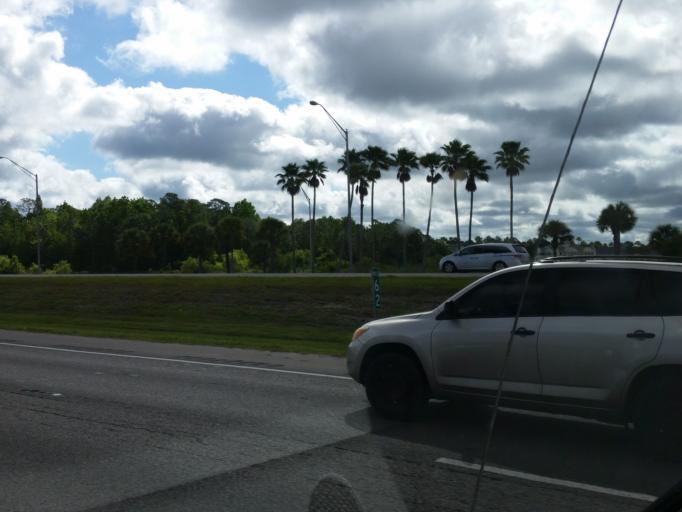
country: US
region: Florida
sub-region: Osceola County
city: Celebration
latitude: 28.3083
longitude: -81.5682
